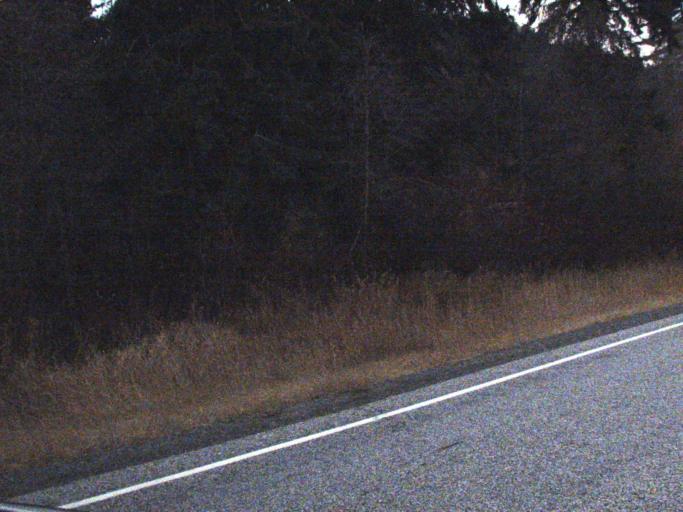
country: US
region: Washington
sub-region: Ferry County
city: Republic
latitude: 48.6166
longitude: -118.6669
